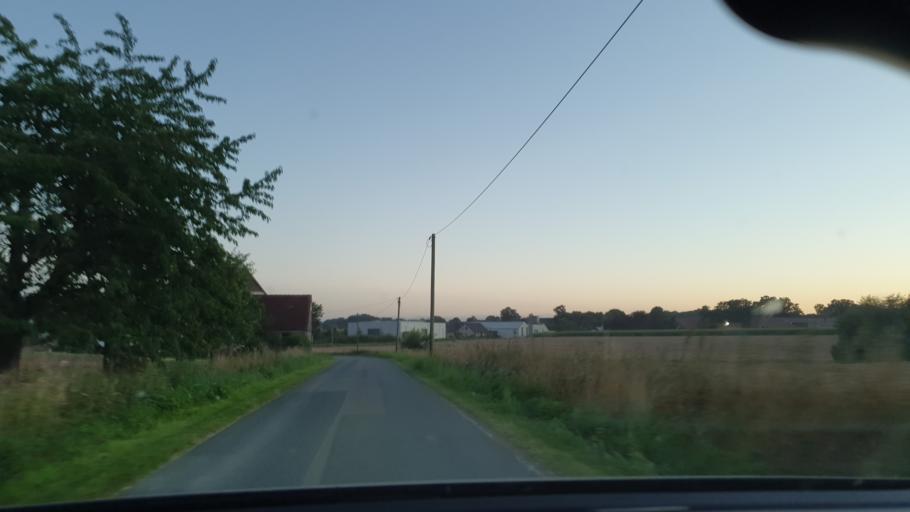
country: DE
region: North Rhine-Westphalia
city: Spenge
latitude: 52.1841
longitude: 8.4805
